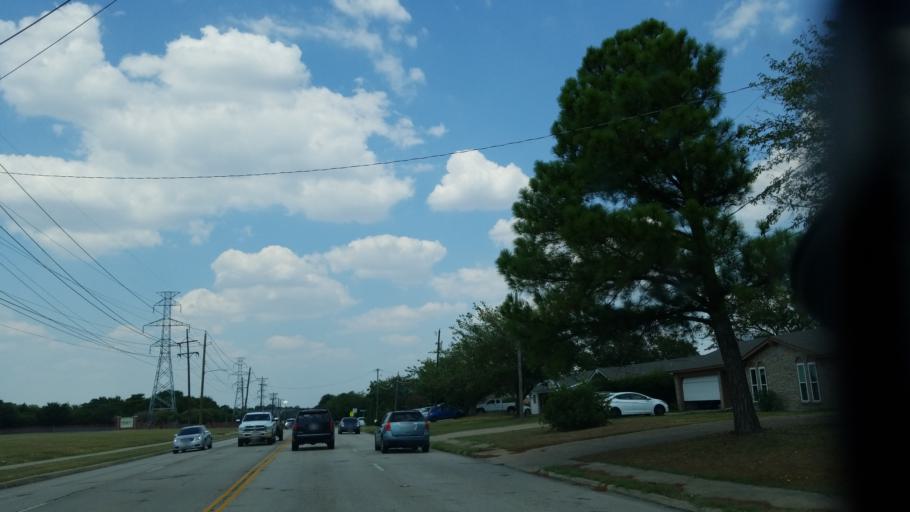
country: US
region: Texas
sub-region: Dallas County
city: Grand Prairie
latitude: 32.7233
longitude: -96.9858
